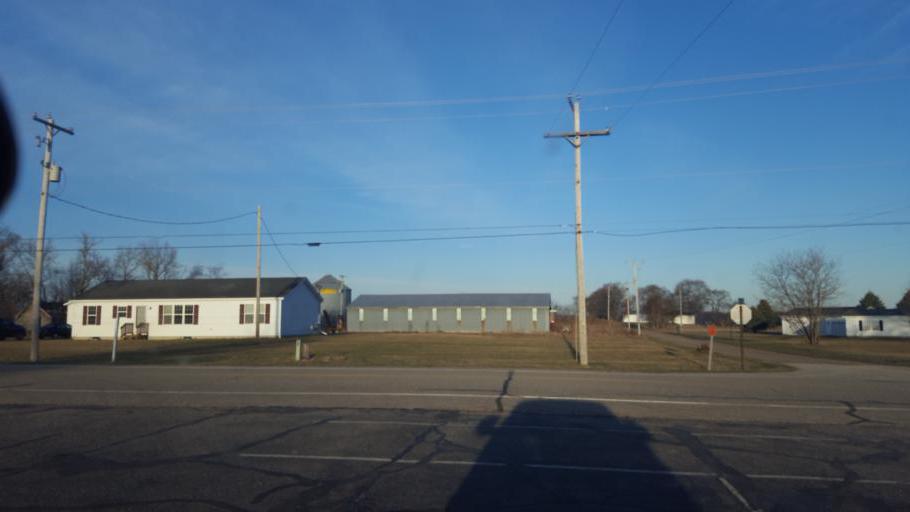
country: US
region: Michigan
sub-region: Montcalm County
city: Edmore
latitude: 43.4555
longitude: -85.0440
